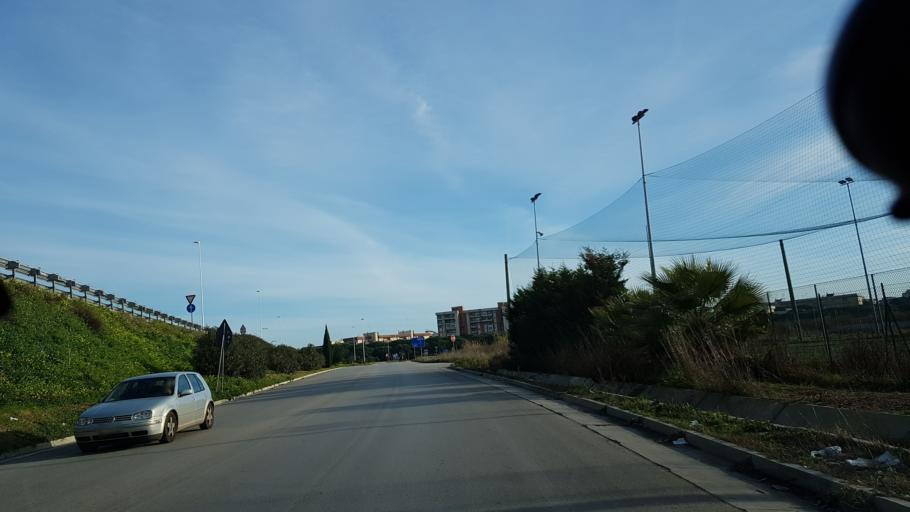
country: IT
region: Apulia
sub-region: Provincia di Brindisi
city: Brindisi
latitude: 40.6249
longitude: 17.9203
